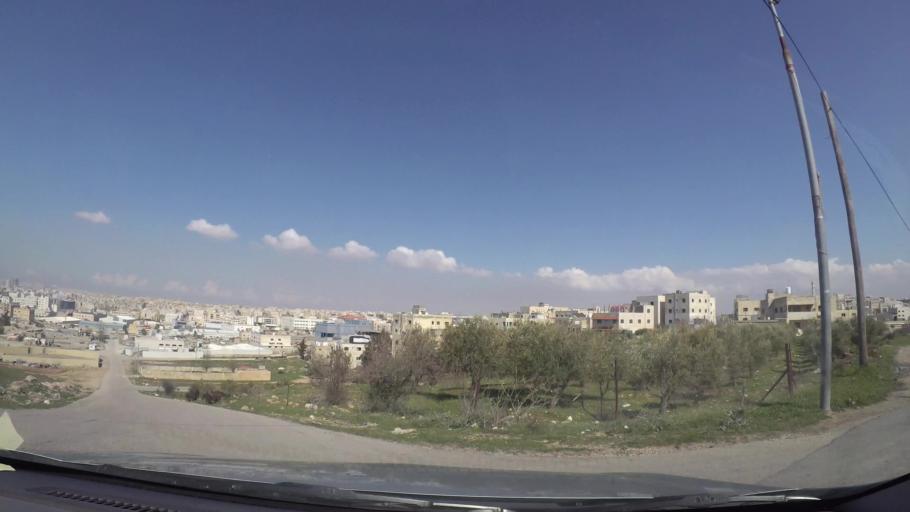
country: JO
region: Amman
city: Al Bunayyat ash Shamaliyah
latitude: 31.9084
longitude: 35.9084
